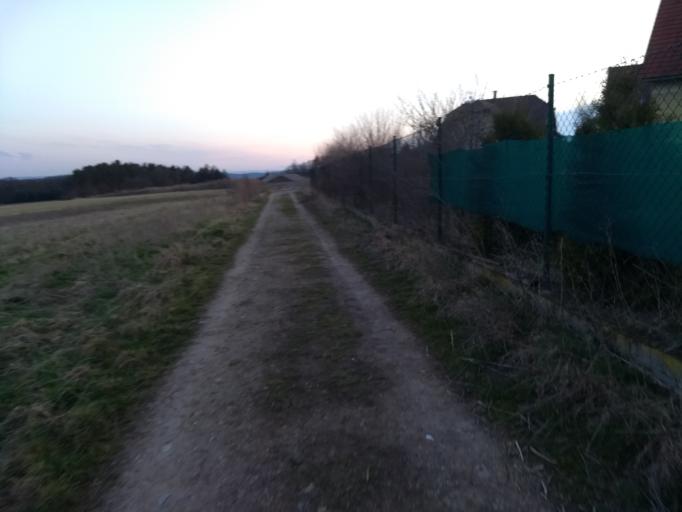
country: CZ
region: Central Bohemia
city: Unhost'
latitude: 50.0493
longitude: 14.1635
